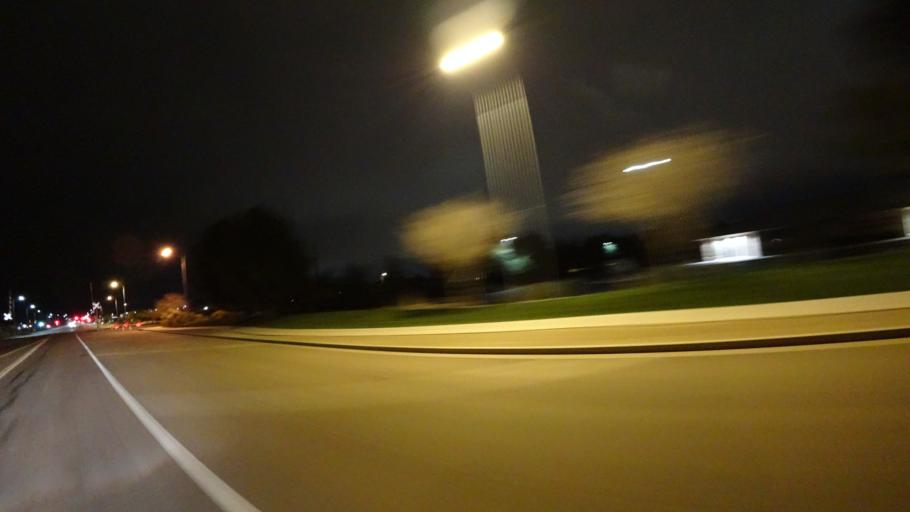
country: US
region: Arizona
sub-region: Maricopa County
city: Sun Lakes
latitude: 33.2332
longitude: -111.8359
